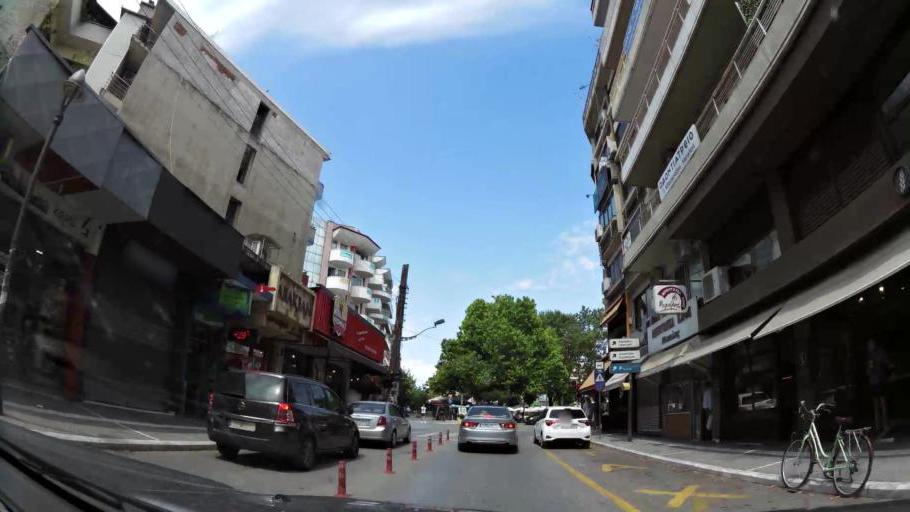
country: GR
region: Central Macedonia
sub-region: Nomos Pierias
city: Katerini
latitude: 40.2709
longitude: 22.5096
